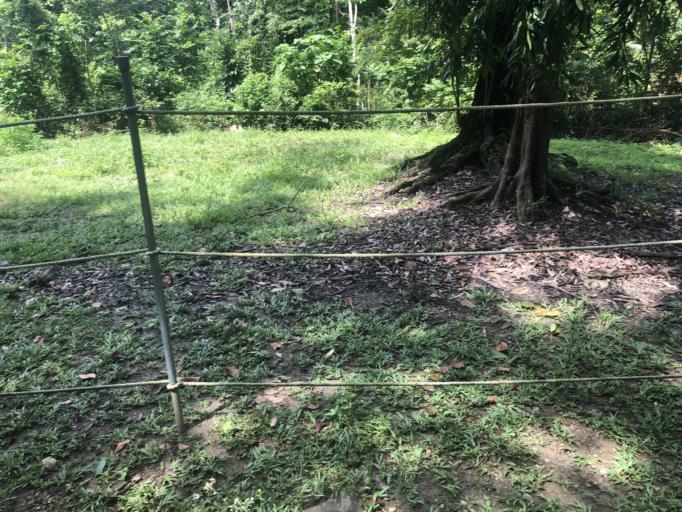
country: TW
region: Taiwan
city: Yujing
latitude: 22.9331
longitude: 120.5921
